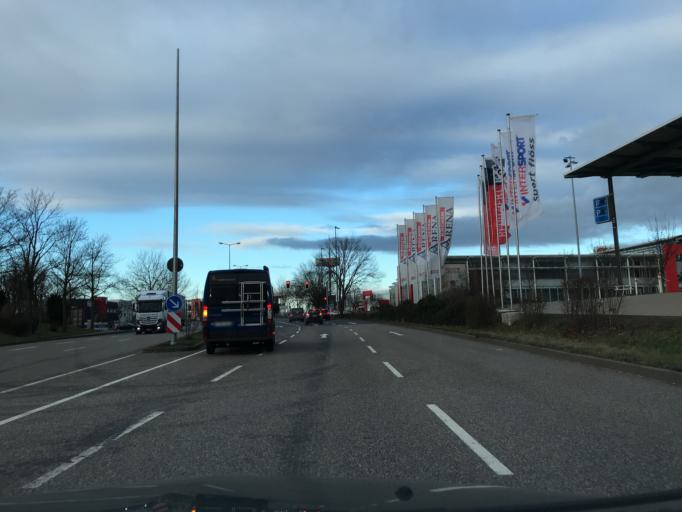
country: DE
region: Baden-Wuerttemberg
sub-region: Regierungsbezirk Stuttgart
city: Waiblingen
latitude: 48.8213
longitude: 9.3008
